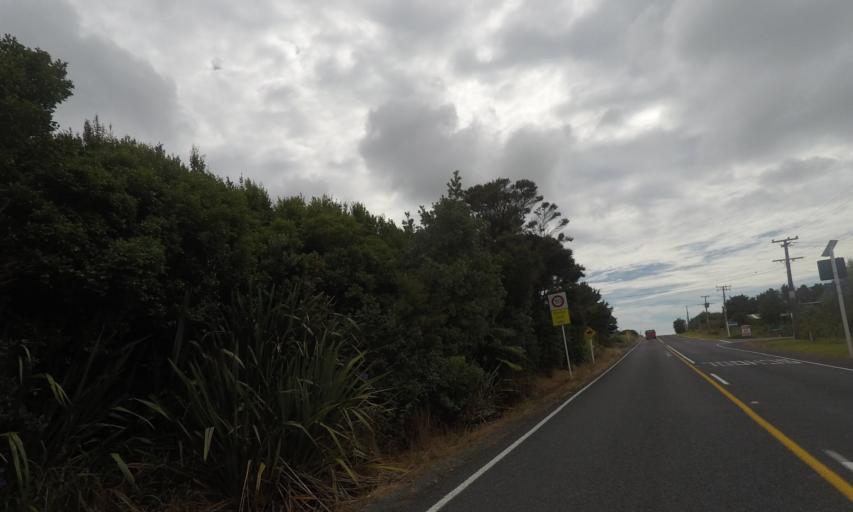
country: NZ
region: Northland
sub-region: Whangarei
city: Ruakaka
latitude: -35.7693
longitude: 174.4815
